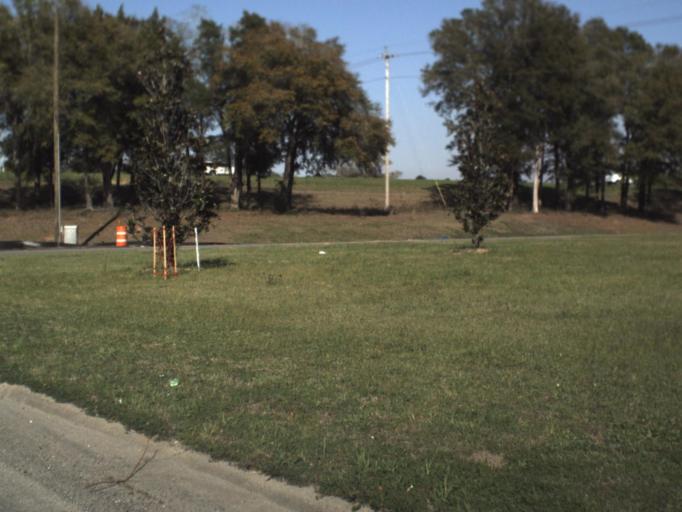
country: US
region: Florida
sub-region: Jackson County
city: Marianna
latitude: 30.7201
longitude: -85.1853
